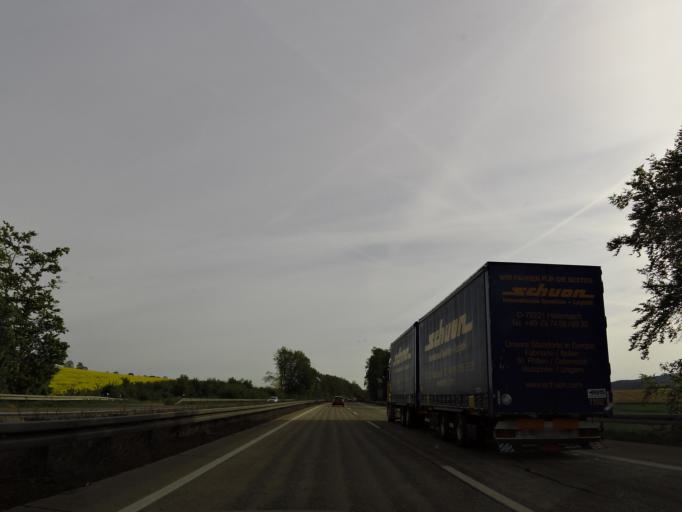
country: DE
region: Lower Saxony
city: Kalefeld
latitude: 51.8032
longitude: 10.0894
